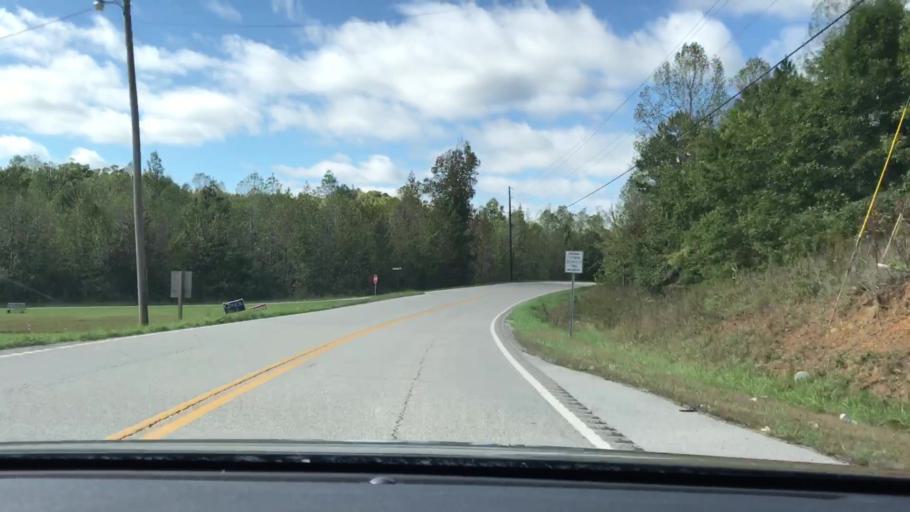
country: US
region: Tennessee
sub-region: Scott County
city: Huntsville
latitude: 36.3355
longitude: -84.6089
